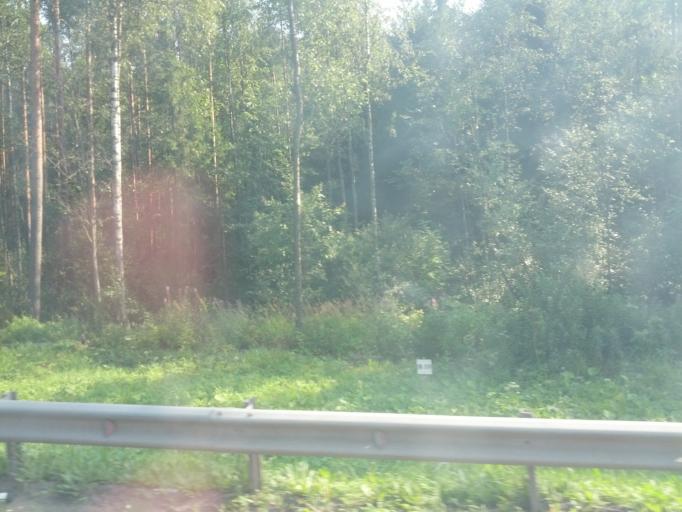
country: RU
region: Leningrad
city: Staraya
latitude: 59.8881
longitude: 30.6024
